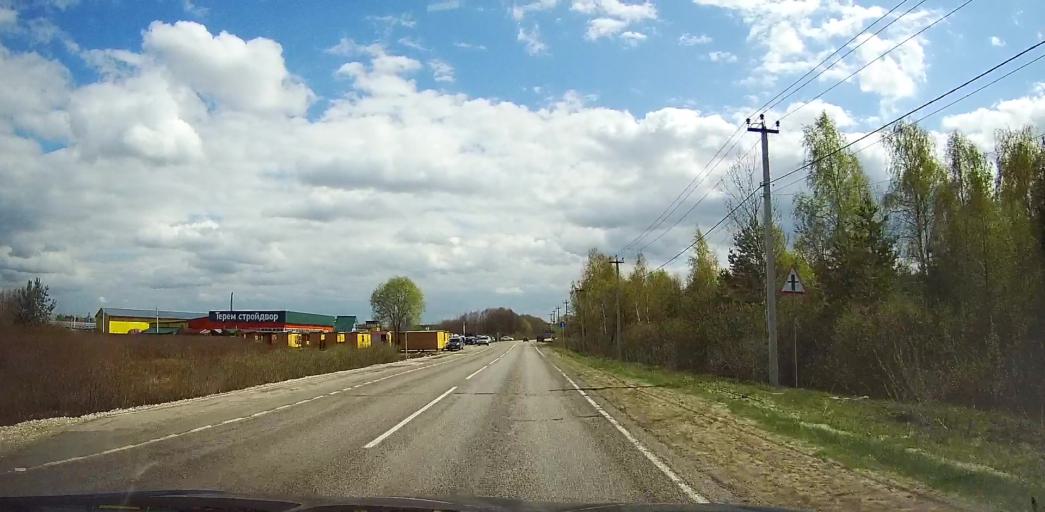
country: RU
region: Moskovskaya
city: Davydovo
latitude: 55.5496
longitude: 38.8032
